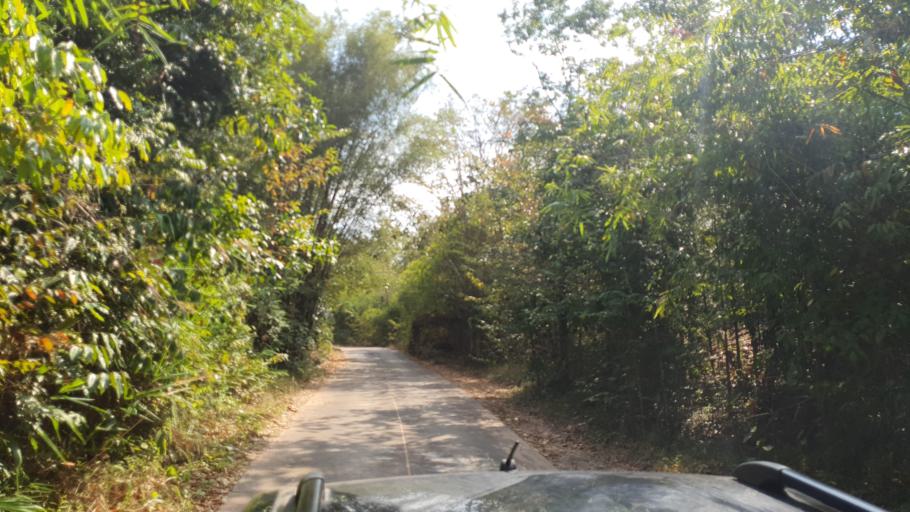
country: TH
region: Changwat Bueng Kan
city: Si Wilai
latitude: 18.2700
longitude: 103.8007
